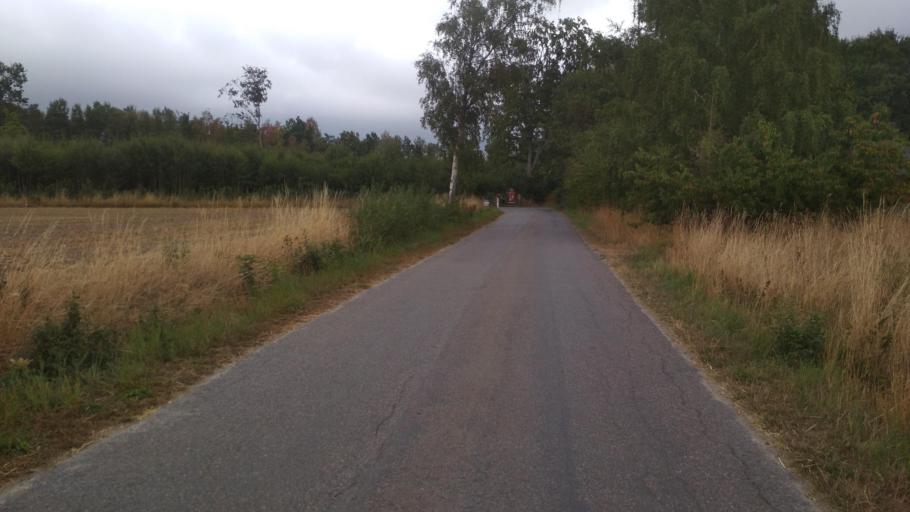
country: DK
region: Capital Region
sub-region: Bornholm Kommune
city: Akirkeby
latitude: 55.0605
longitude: 14.9490
